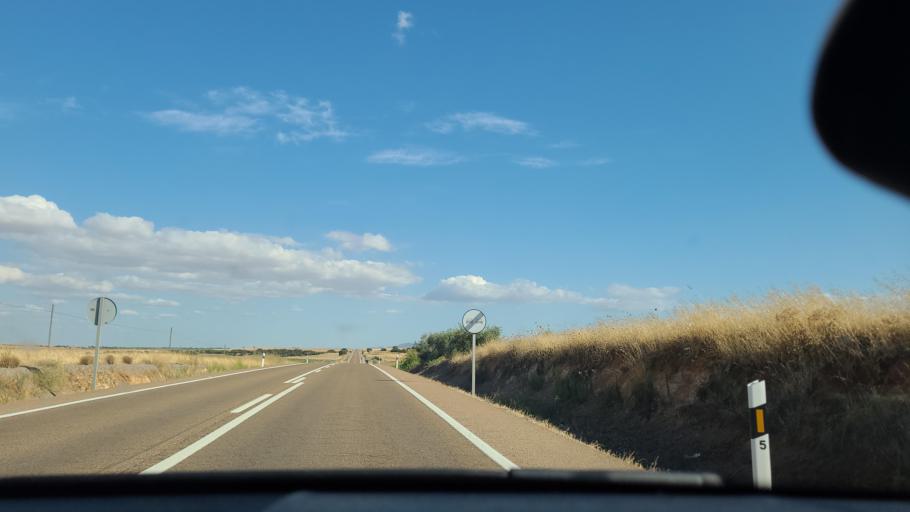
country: ES
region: Extremadura
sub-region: Provincia de Badajoz
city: Usagre
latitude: 38.3368
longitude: -6.1580
